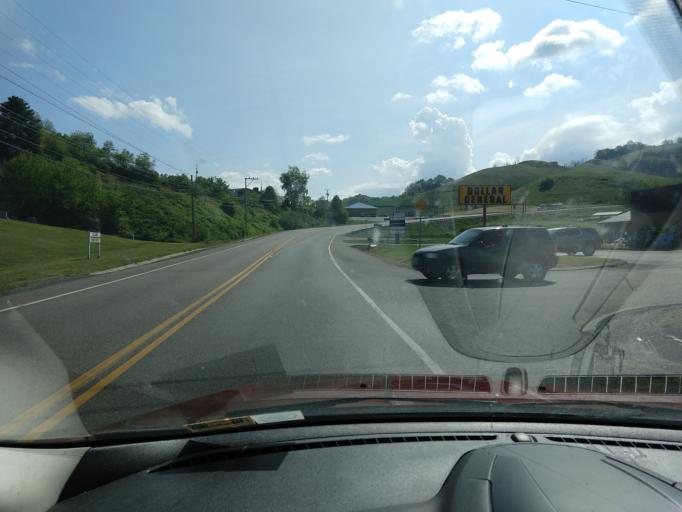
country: US
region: Virginia
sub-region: Russell County
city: Honaker
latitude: 37.0157
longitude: -81.9589
